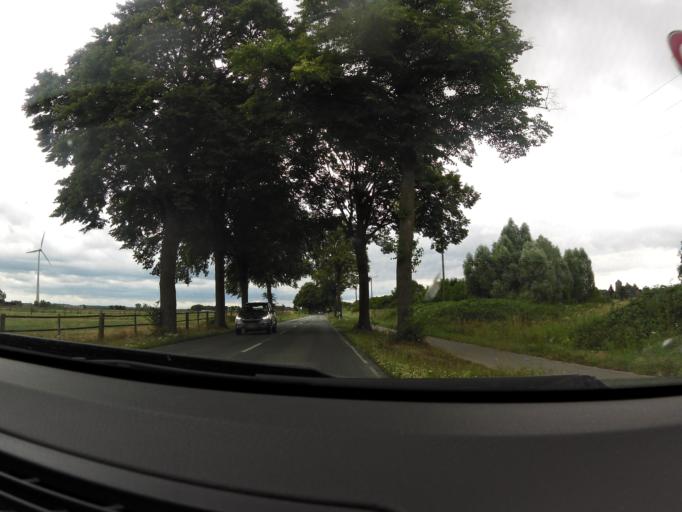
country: DE
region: North Rhine-Westphalia
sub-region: Regierungsbezirk Dusseldorf
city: Xanten
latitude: 51.6125
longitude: 6.4680
